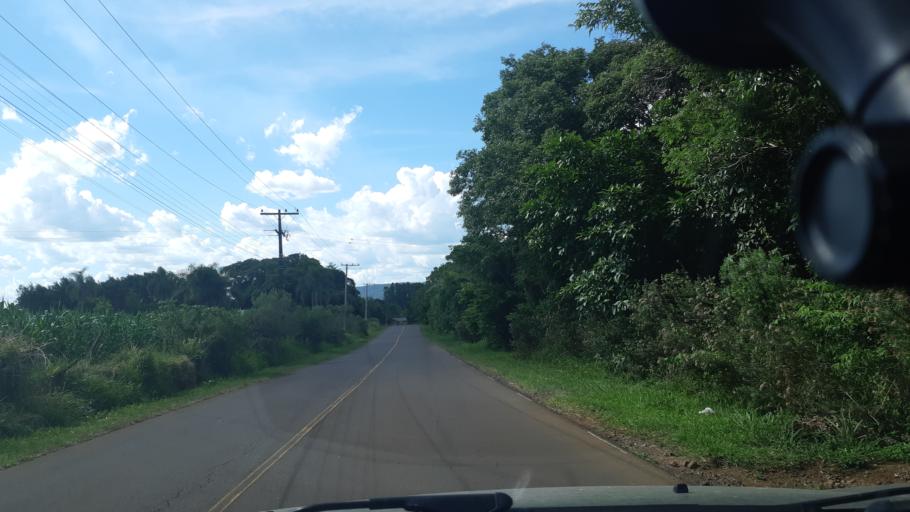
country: BR
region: Rio Grande do Sul
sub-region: Novo Hamburgo
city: Novo Hamburgo
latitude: -29.6251
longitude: -51.1089
